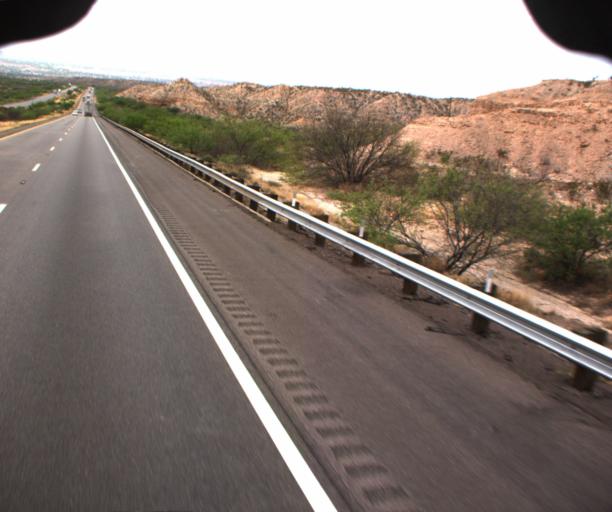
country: US
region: Arizona
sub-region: Cochise County
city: Saint David
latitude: 31.9819
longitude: -110.2117
